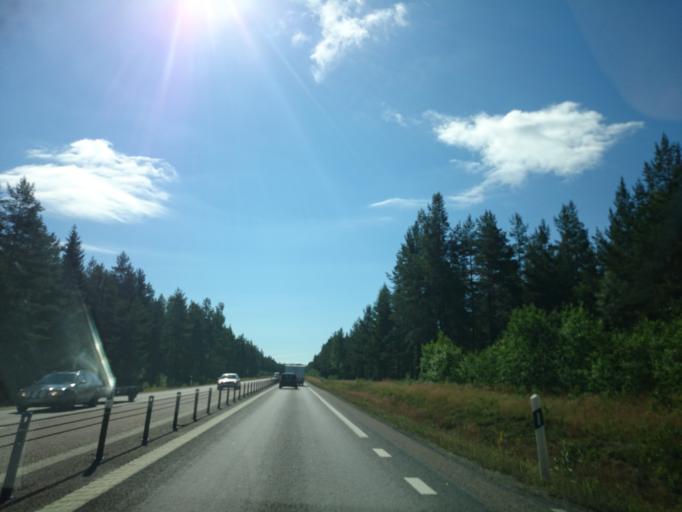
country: SE
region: Gaevleborg
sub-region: Gavle Kommun
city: Norrsundet
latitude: 60.9937
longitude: 16.9998
